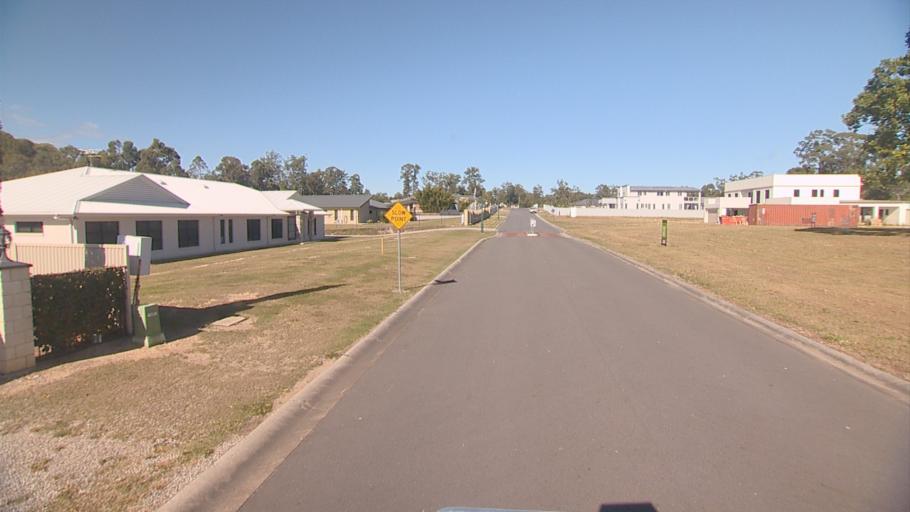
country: AU
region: Queensland
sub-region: Brisbane
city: Forest Lake
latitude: -27.6586
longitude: 153.0132
